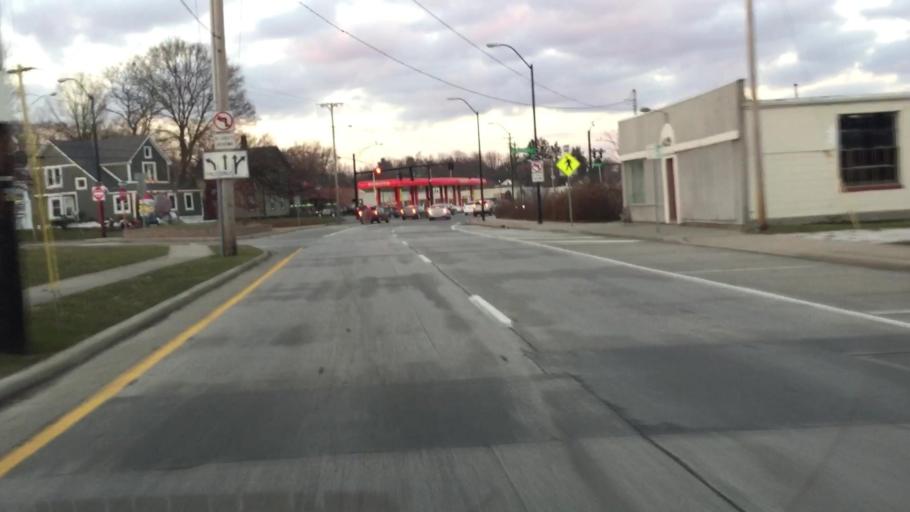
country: US
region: Ohio
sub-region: Portage County
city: Kent
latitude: 41.1575
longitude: -81.3601
